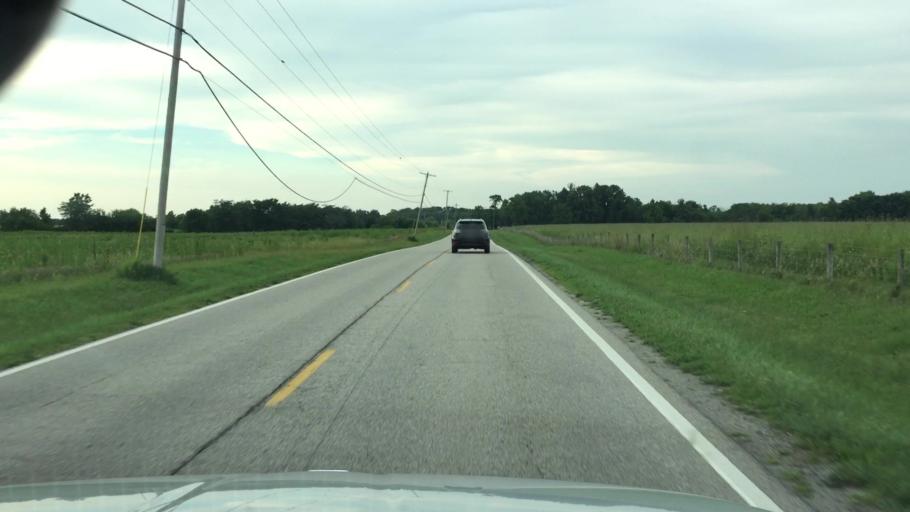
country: US
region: Ohio
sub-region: Madison County
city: West Jefferson
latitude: 39.9911
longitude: -83.2640
